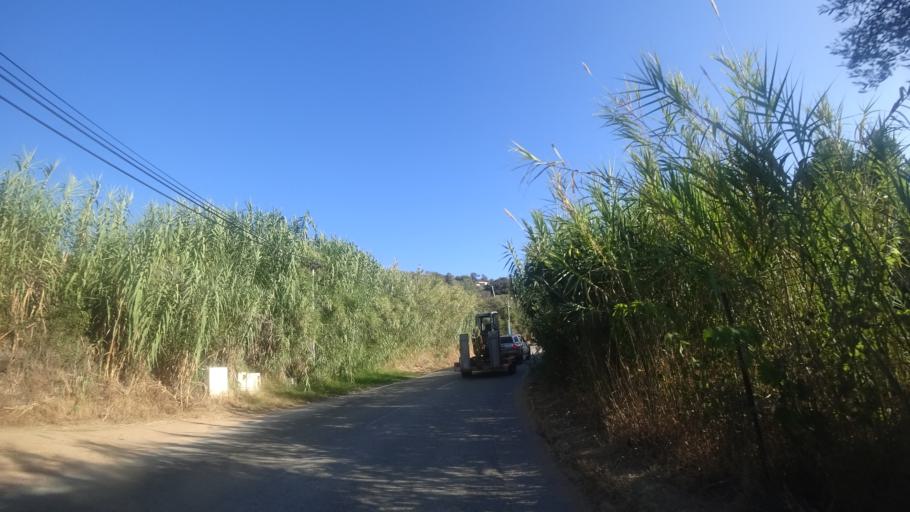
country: FR
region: Corsica
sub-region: Departement de la Corse-du-Sud
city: Cargese
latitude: 42.1440
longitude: 8.6028
